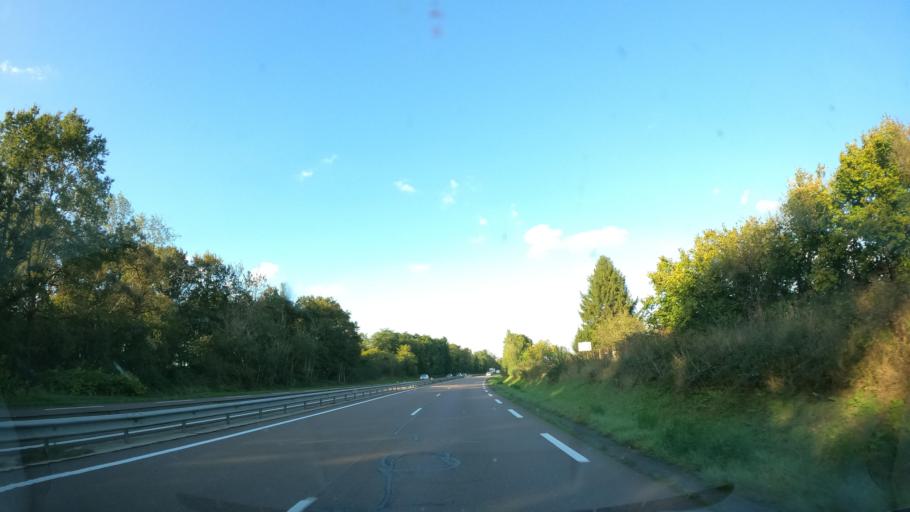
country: FR
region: Bourgogne
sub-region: Departement de Saone-et-Loire
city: Montceau-les-Mines
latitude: 46.6577
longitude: 4.3309
